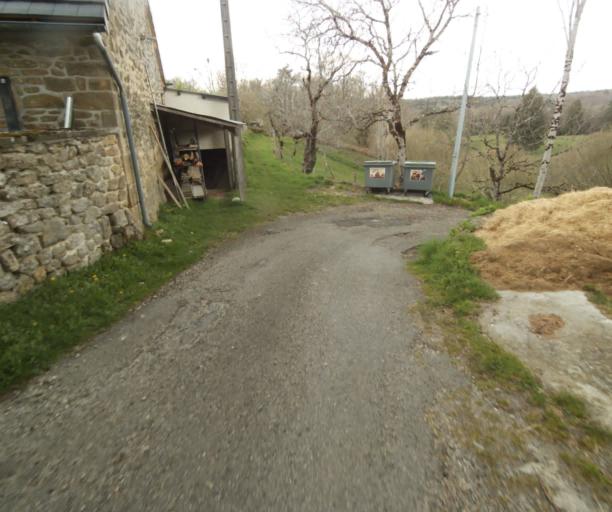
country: FR
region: Limousin
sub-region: Departement de la Correze
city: Laguenne
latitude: 45.2481
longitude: 1.8938
